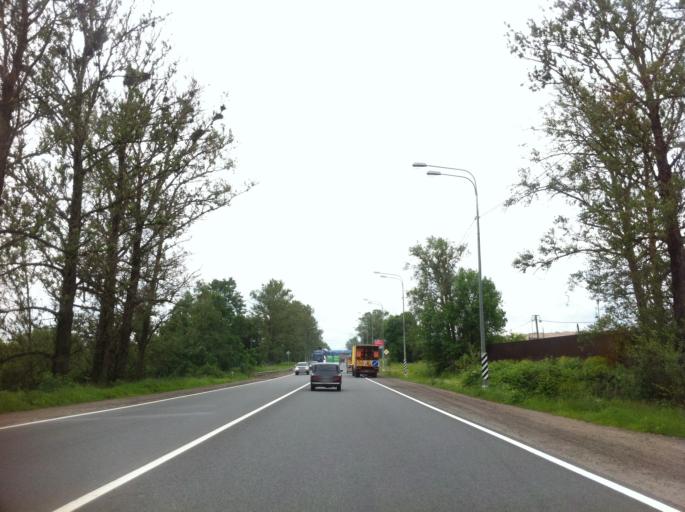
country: RU
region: Leningrad
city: Maloye Verevo
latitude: 59.6183
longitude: 30.1781
